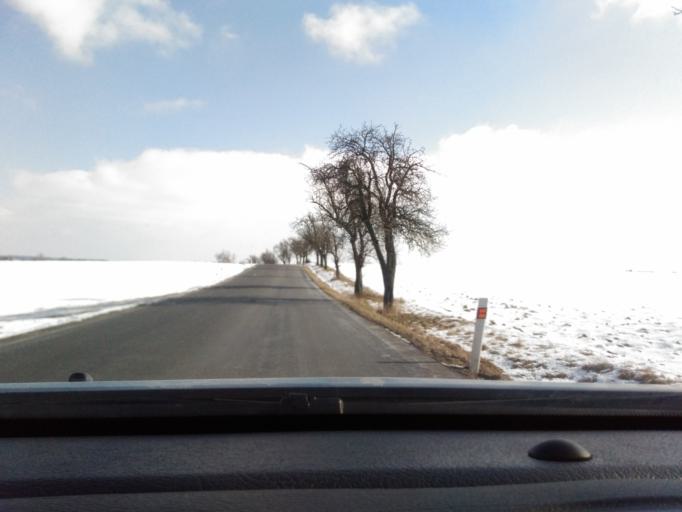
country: CZ
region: Vysocina
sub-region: Okres Zd'ar nad Sazavou
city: Velka Bites
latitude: 49.3221
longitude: 16.1546
